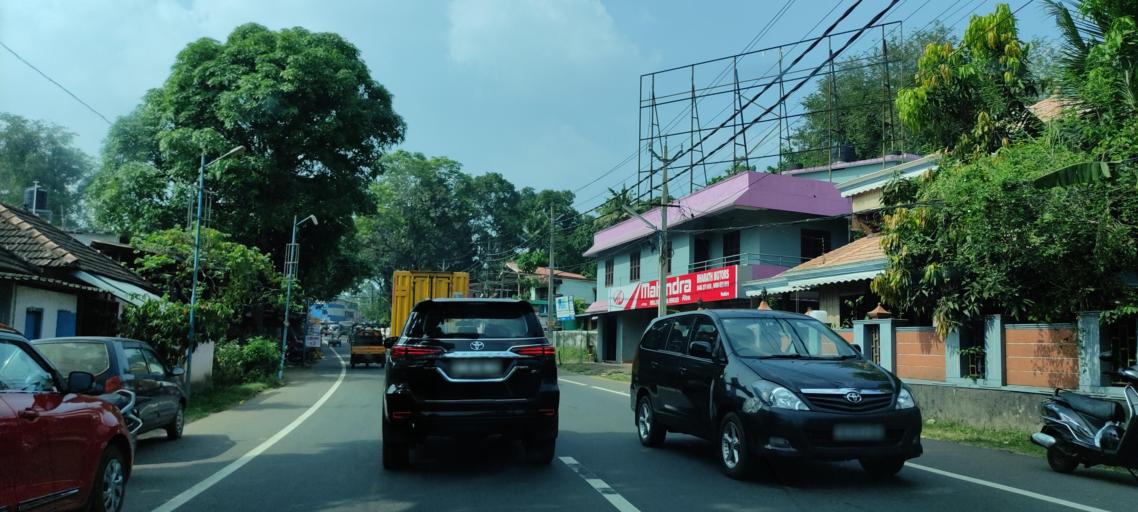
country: IN
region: Kerala
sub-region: Pattanamtitta
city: Adur
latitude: 9.2306
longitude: 76.6767
